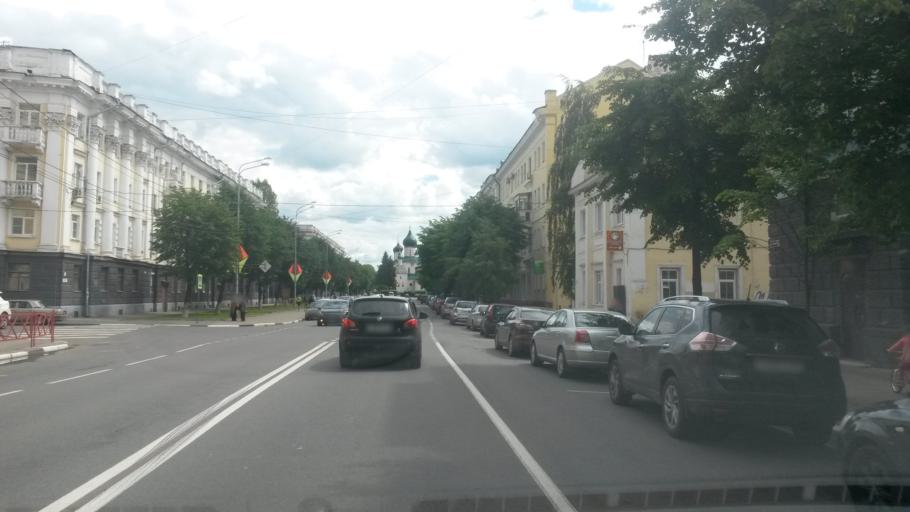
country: RU
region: Jaroslavl
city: Yaroslavl
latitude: 57.6297
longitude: 39.8914
